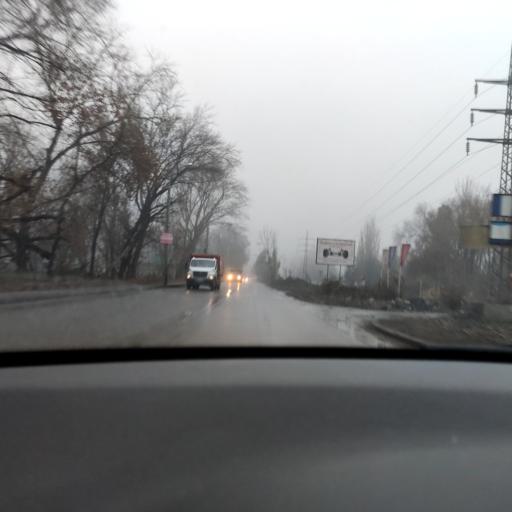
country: RU
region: Samara
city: Samara
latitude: 53.1919
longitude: 50.2526
